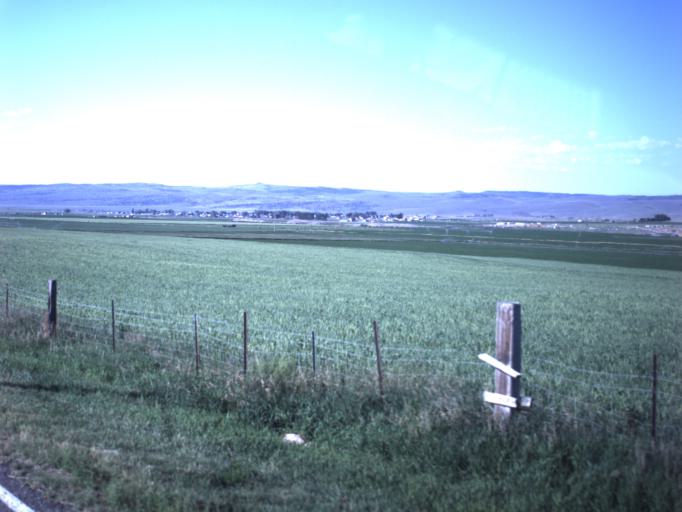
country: US
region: Utah
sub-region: Wayne County
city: Loa
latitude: 38.4312
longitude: -111.6203
